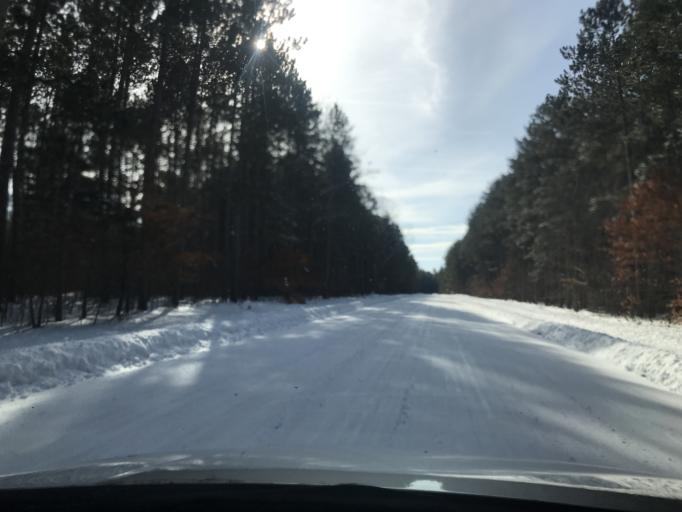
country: US
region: Wisconsin
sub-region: Oconto County
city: Gillett
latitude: 45.1406
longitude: -88.2472
